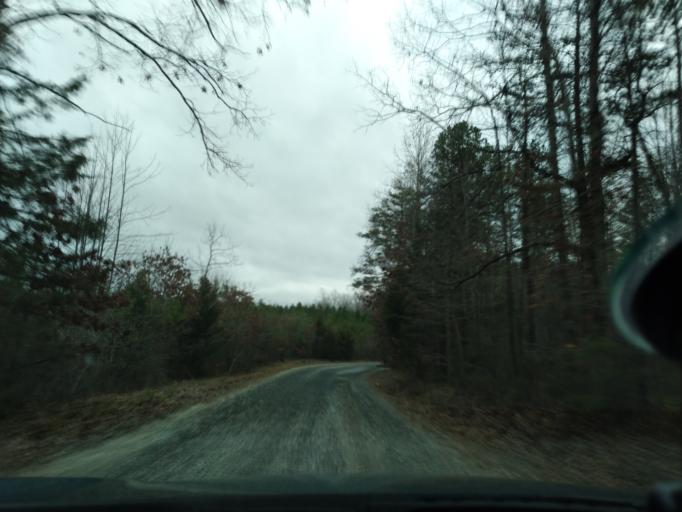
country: US
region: Virginia
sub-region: Buckingham County
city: Buckingham
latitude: 37.4300
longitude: -78.6562
